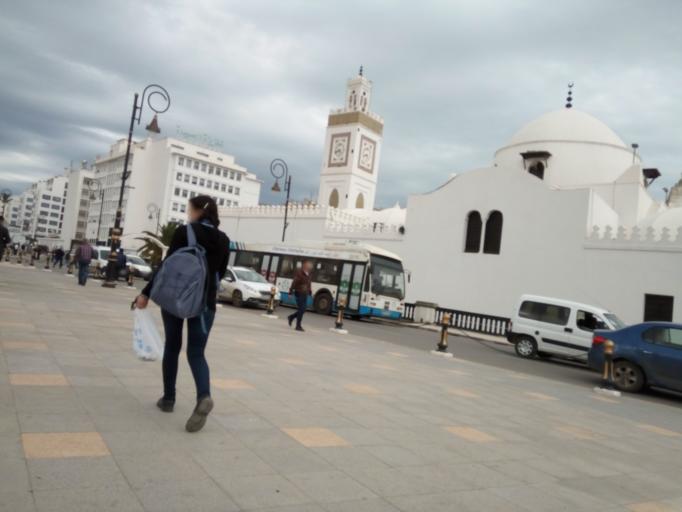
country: DZ
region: Alger
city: Algiers
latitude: 36.7846
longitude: 3.0627
